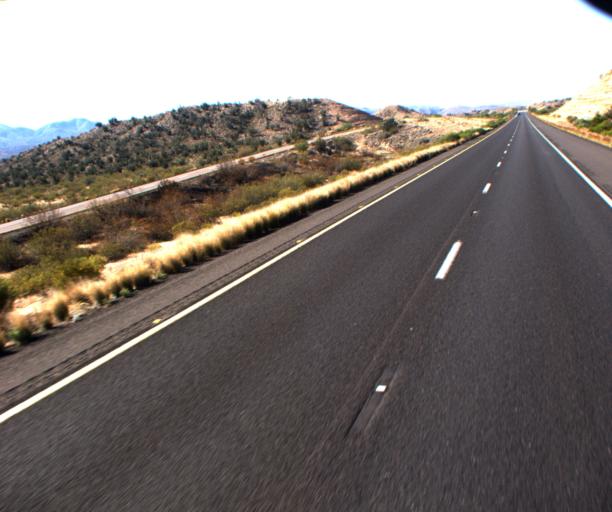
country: US
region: Arizona
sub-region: Mohave County
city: Kingman
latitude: 35.0853
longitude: -113.6662
